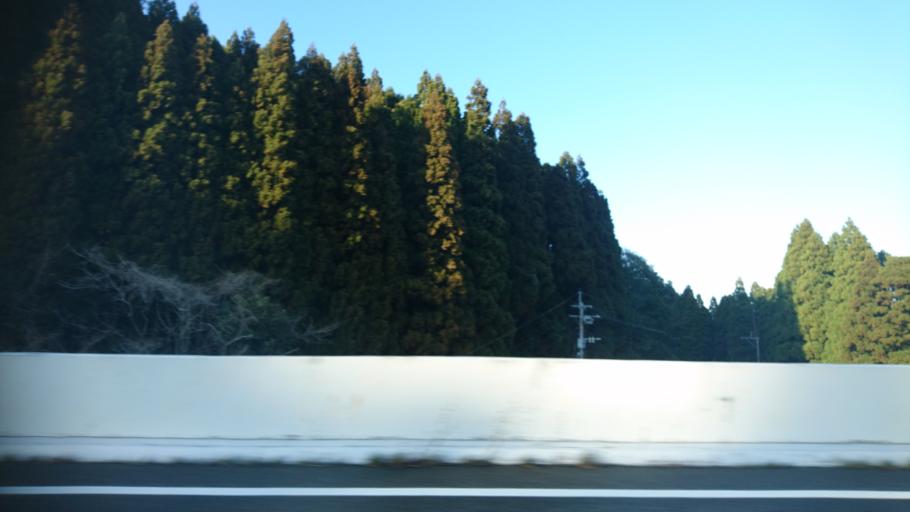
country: JP
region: Miyazaki
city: Miyazaki-shi
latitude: 31.8188
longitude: 131.2637
